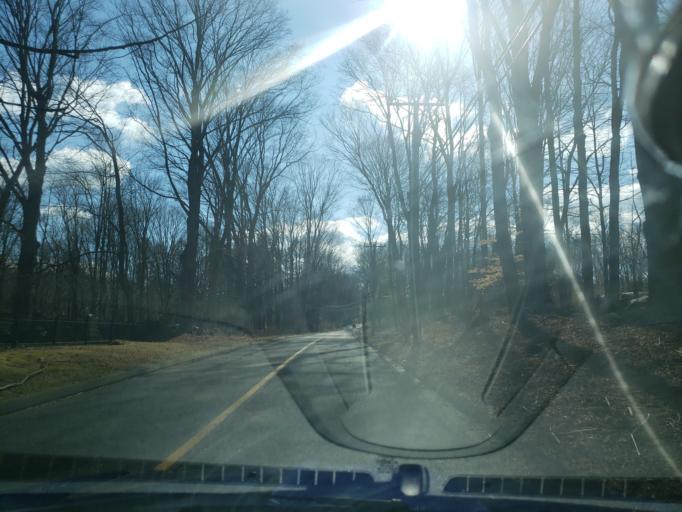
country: US
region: Connecticut
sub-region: Fairfield County
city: Bethel
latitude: 41.3590
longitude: -73.3792
